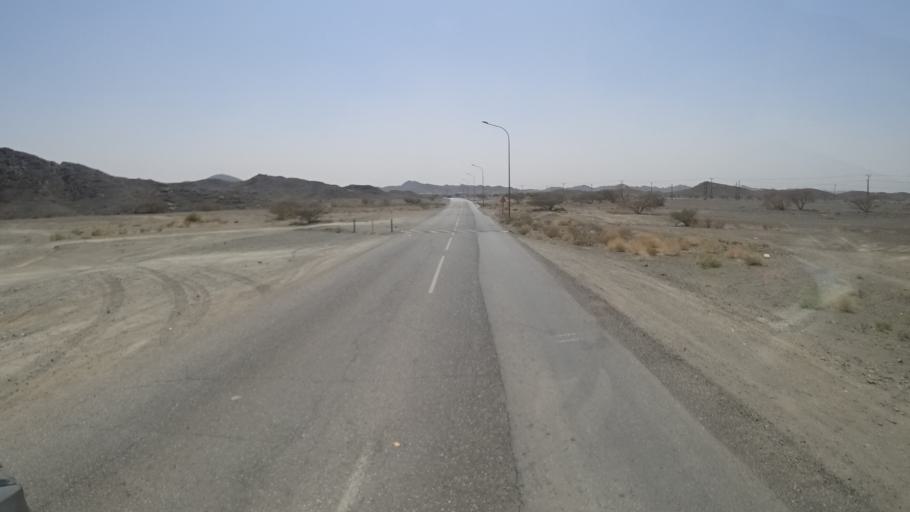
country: OM
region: Ash Sharqiyah
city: Ibra'
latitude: 22.6629
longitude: 58.5279
